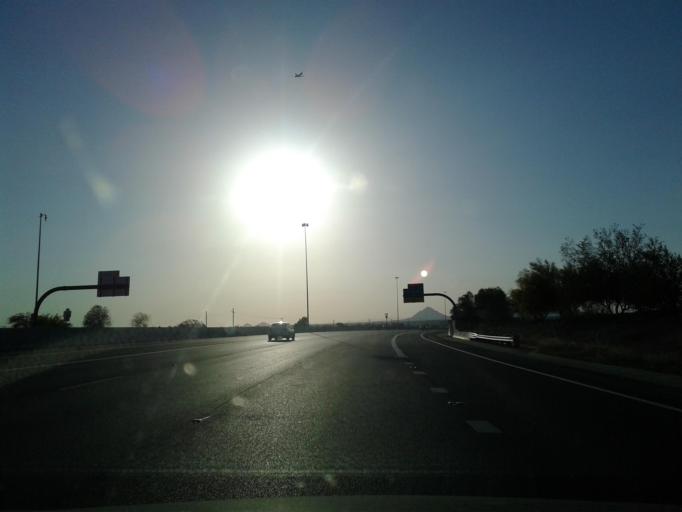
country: US
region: Arizona
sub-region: Maricopa County
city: Mesa
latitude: 33.4799
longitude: -111.7459
